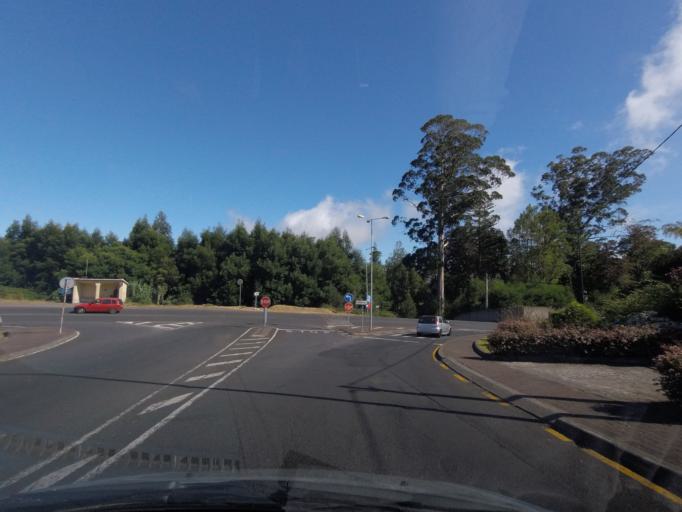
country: PT
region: Madeira
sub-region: Santa Cruz
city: Camacha
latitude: 32.6777
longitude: -16.8453
